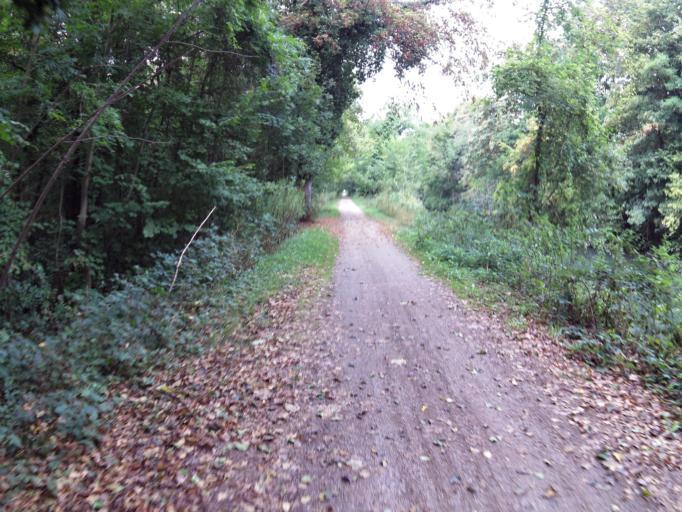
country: FR
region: Alsace
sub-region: Departement du Bas-Rhin
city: Marckolsheim
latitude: 48.1311
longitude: 7.5337
